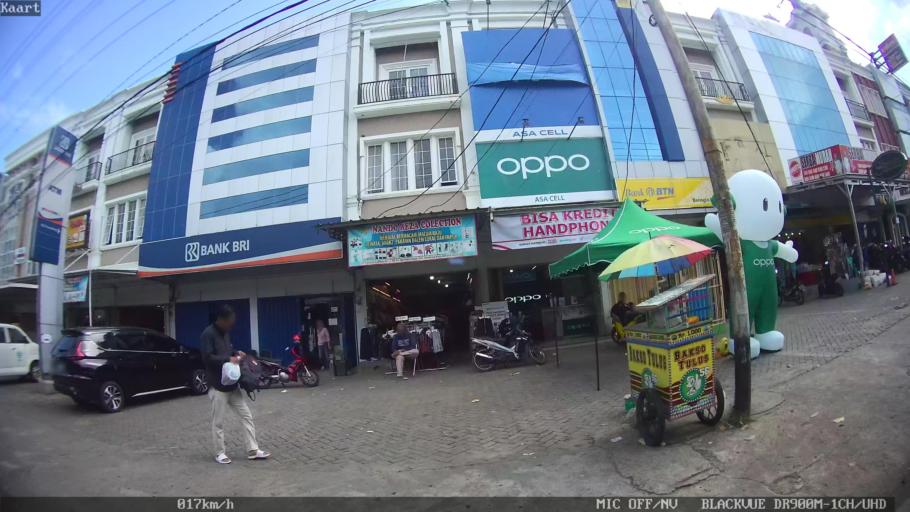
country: ID
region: Lampung
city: Kedaton
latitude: -5.4003
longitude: 105.2103
